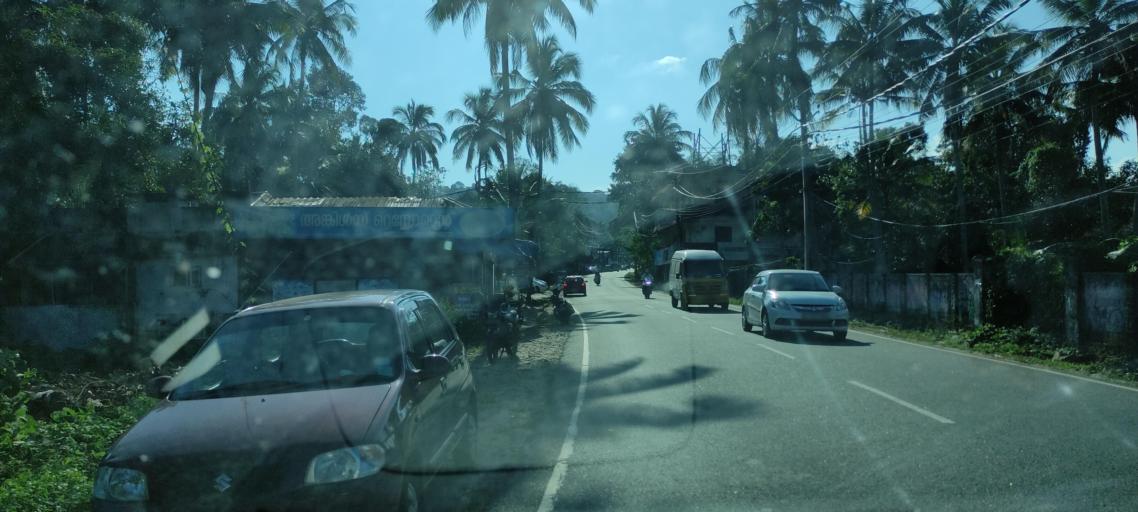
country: IN
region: Kerala
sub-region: Pattanamtitta
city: Pathanamthitta
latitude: 9.2557
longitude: 76.7709
